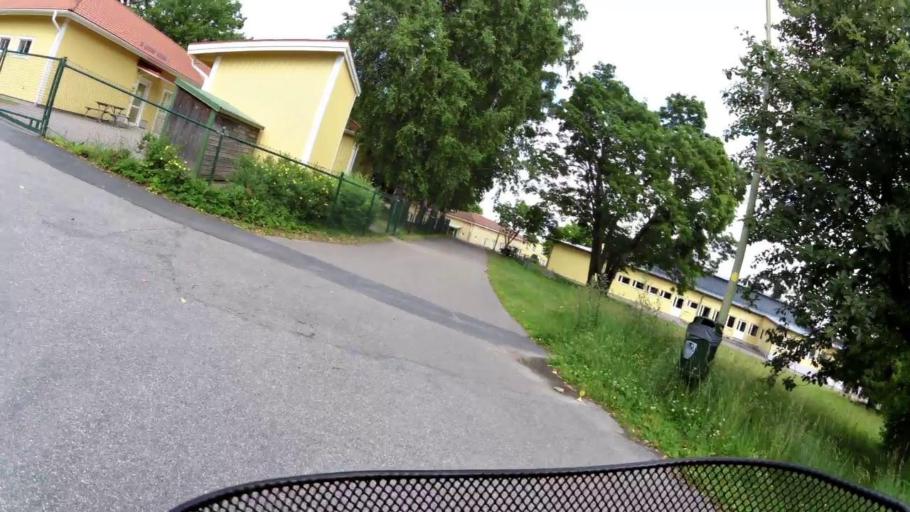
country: SE
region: OEstergoetland
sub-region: Linkopings Kommun
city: Malmslatt
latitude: 58.4162
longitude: 15.5162
